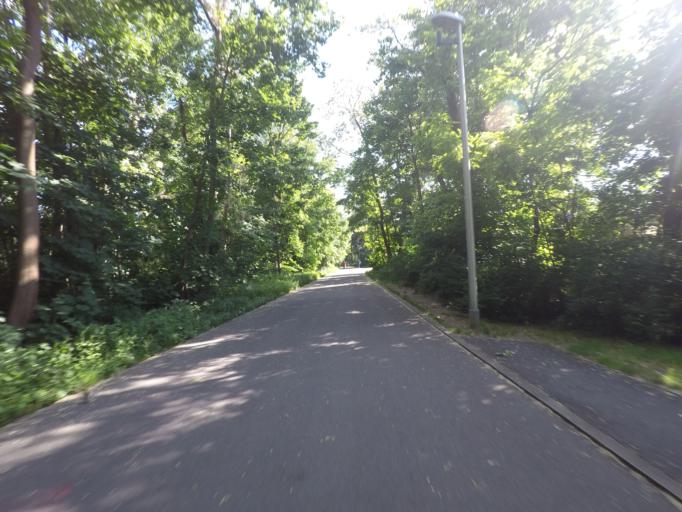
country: DE
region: Brandenburg
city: Eberswalde
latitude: 52.8497
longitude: 13.8244
